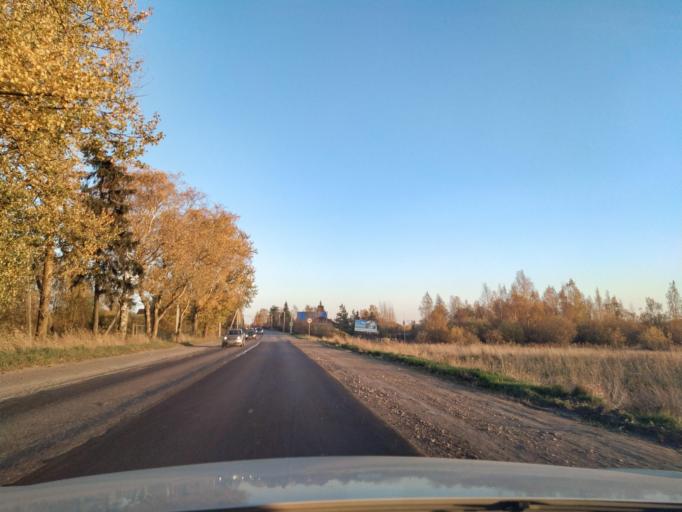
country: RU
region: Leningrad
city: Maloye Verevo
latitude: 59.6151
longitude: 30.2173
